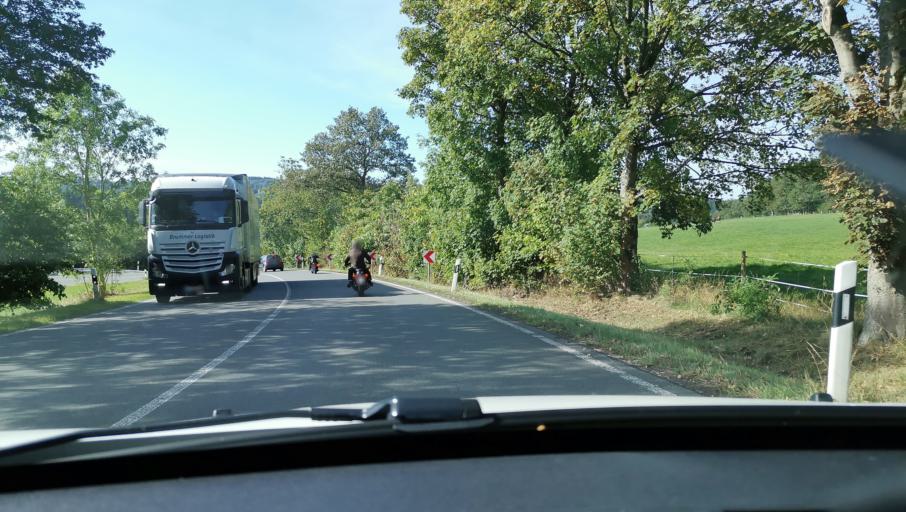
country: DE
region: North Rhine-Westphalia
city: Kierspe
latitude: 51.1462
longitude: 7.5773
